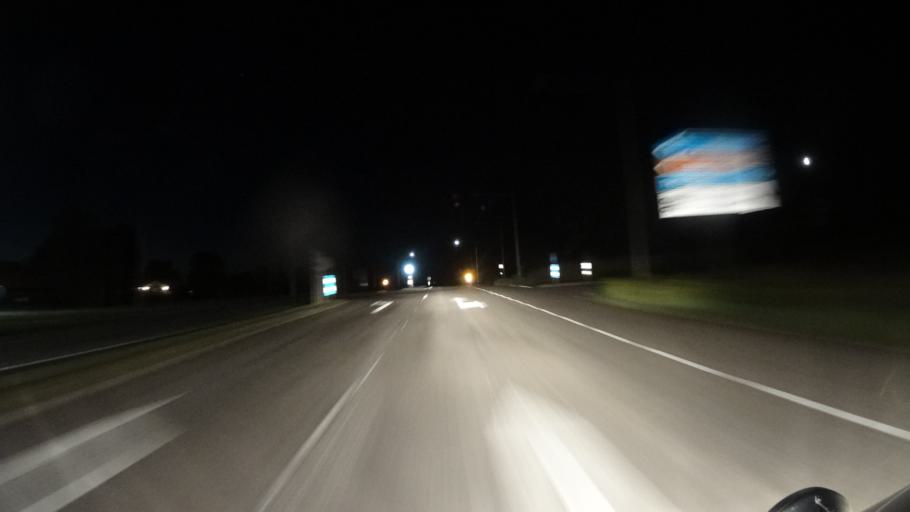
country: SE
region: OEstergoetland
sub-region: Vadstena Kommun
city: Herrestad
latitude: 58.2931
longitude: 14.7876
